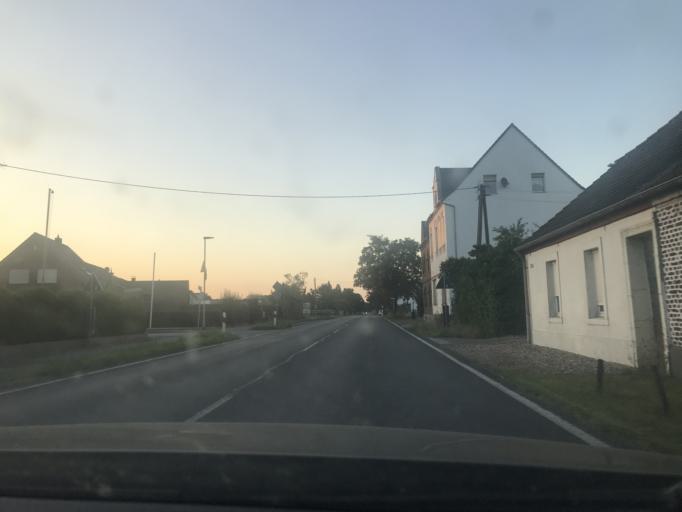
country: DE
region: North Rhine-Westphalia
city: Rheinberg
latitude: 51.5282
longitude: 6.6047
